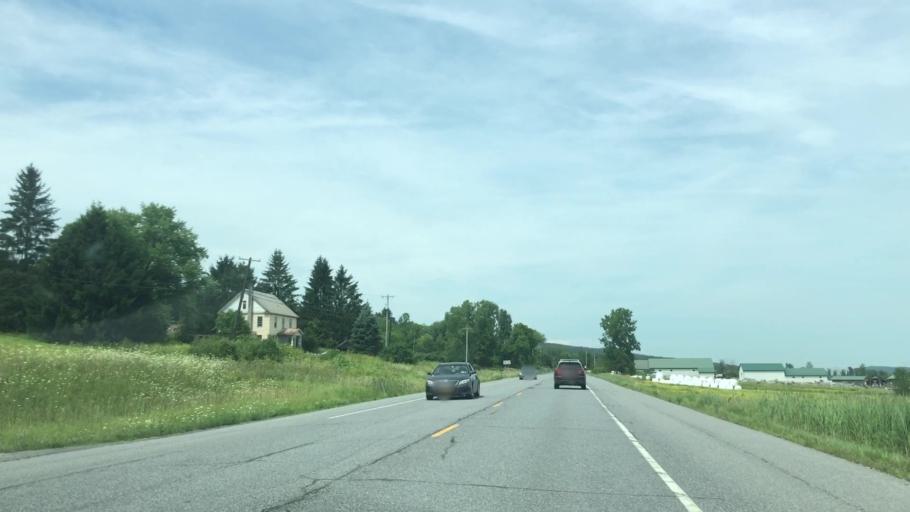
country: US
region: New York
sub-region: Washington County
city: Whitehall
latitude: 43.4771
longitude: -73.4314
